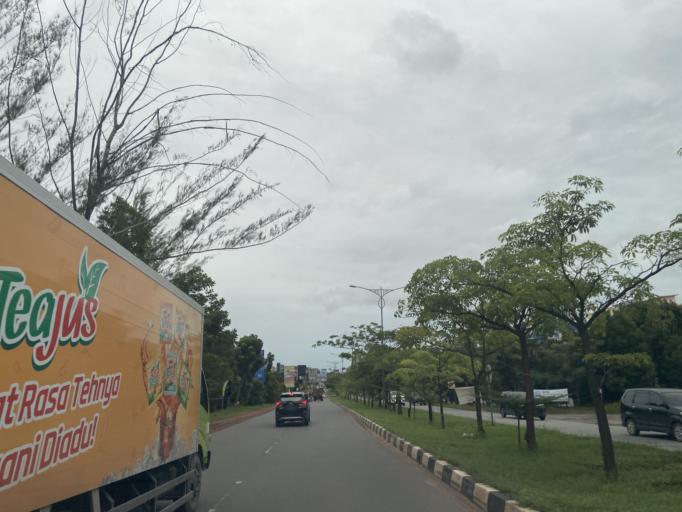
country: SG
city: Singapore
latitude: 1.1196
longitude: 104.0580
